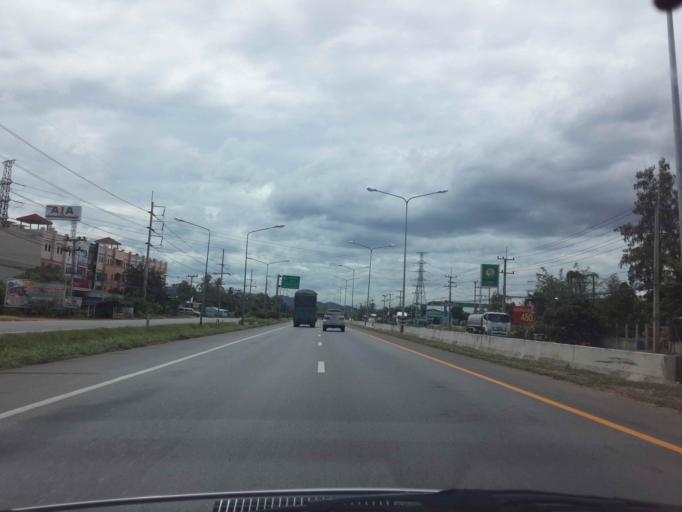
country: TH
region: Phetchaburi
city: Phetchaburi
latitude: 13.1291
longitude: 99.8698
